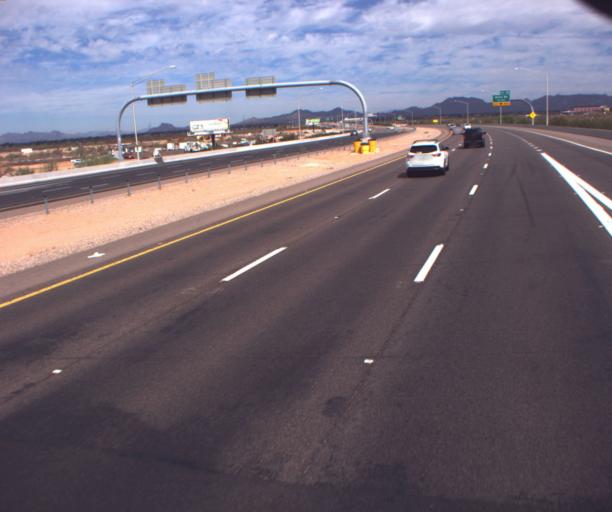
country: US
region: Arizona
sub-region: Maricopa County
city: Queen Creek
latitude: 33.3383
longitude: -111.6447
